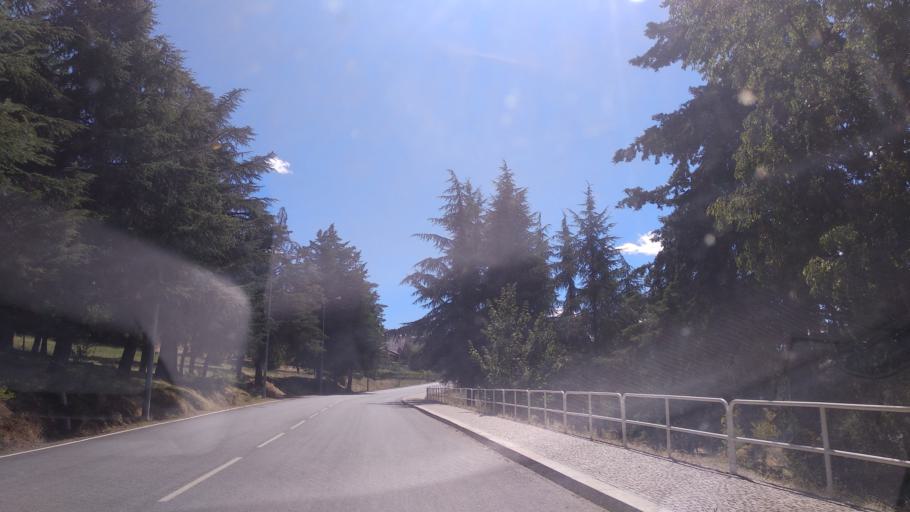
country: PT
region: Braganca
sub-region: Braganca Municipality
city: Braganca
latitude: 41.7974
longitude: -6.7603
